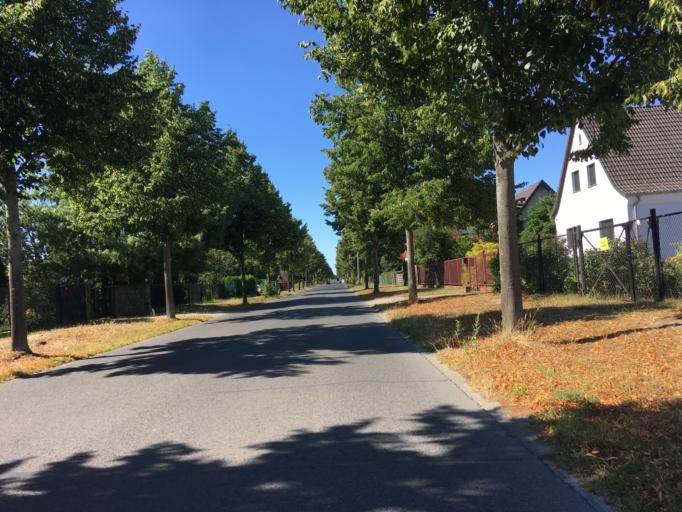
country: DE
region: Brandenburg
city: Schulzendorf
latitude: 52.3571
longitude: 13.5878
